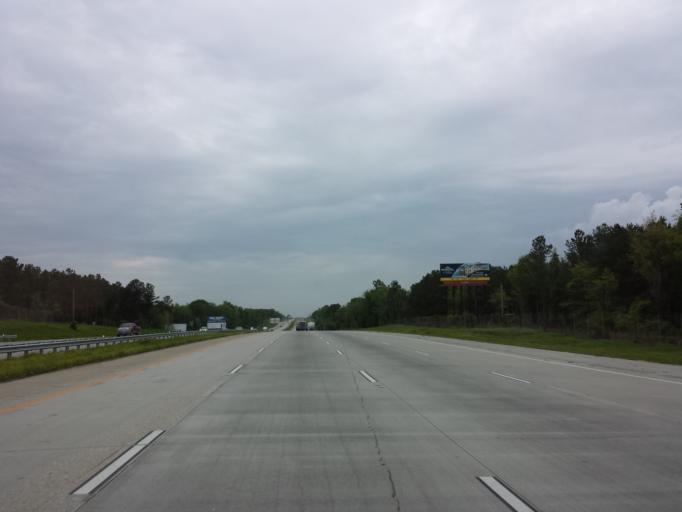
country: US
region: Georgia
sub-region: Dooly County
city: Unadilla
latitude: 32.2643
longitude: -83.7506
